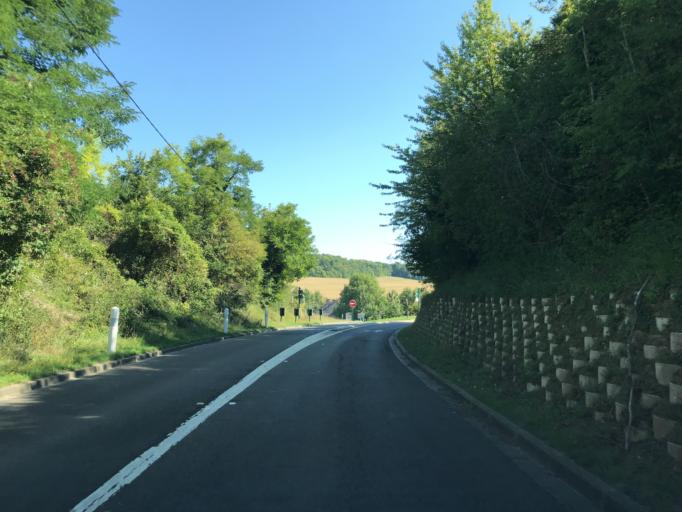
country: FR
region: Haute-Normandie
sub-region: Departement de l'Eure
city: Gasny
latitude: 49.1421
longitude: 1.6694
